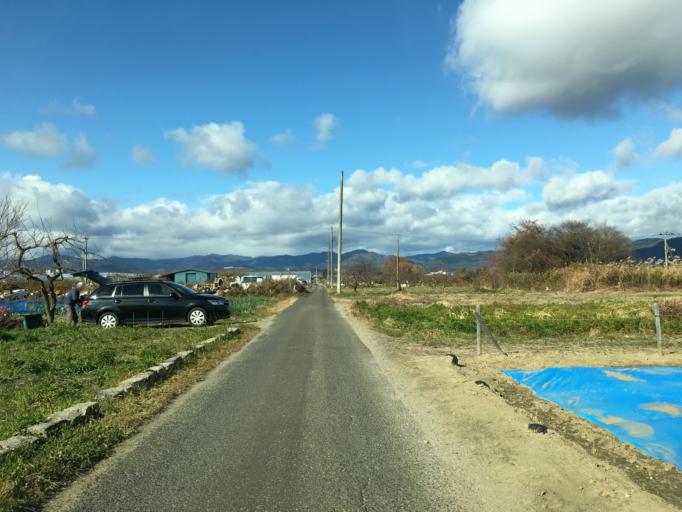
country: JP
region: Fukushima
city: Fukushima-shi
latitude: 37.7874
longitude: 140.5001
